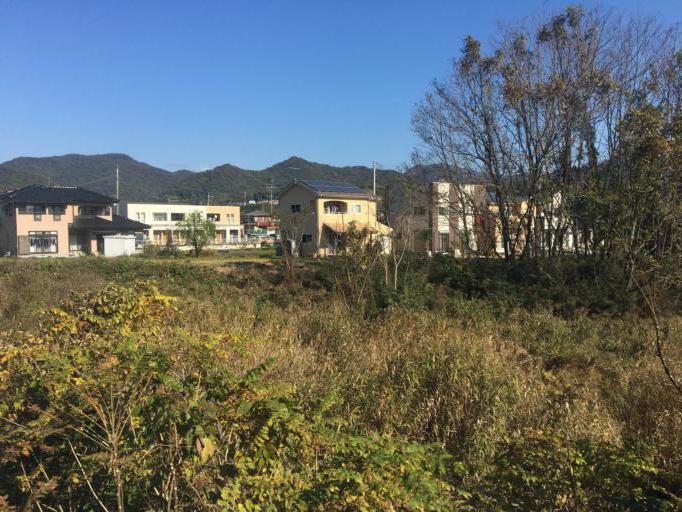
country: JP
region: Gunma
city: Kiryu
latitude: 36.3817
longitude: 139.3634
